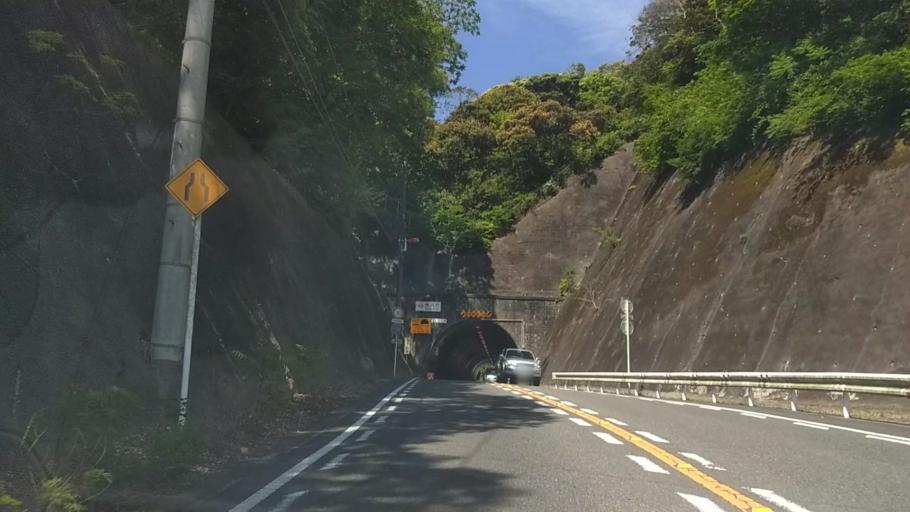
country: JP
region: Kanagawa
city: Zushi
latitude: 35.3160
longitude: 139.6028
